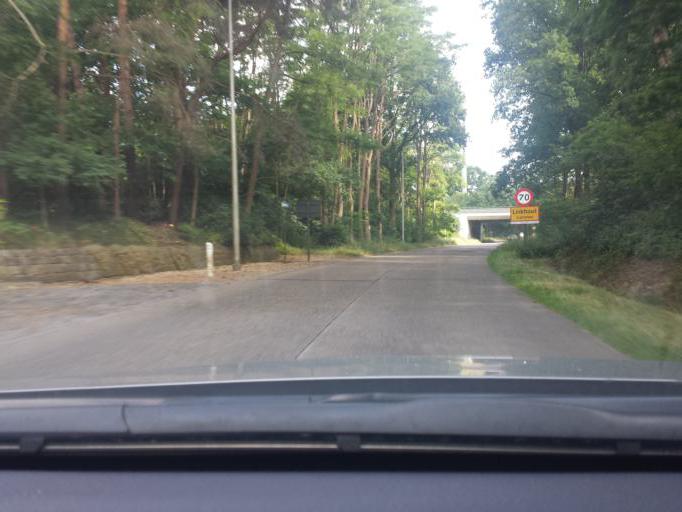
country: BE
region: Flanders
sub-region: Provincie Limburg
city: Halen
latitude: 50.9727
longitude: 5.1259
